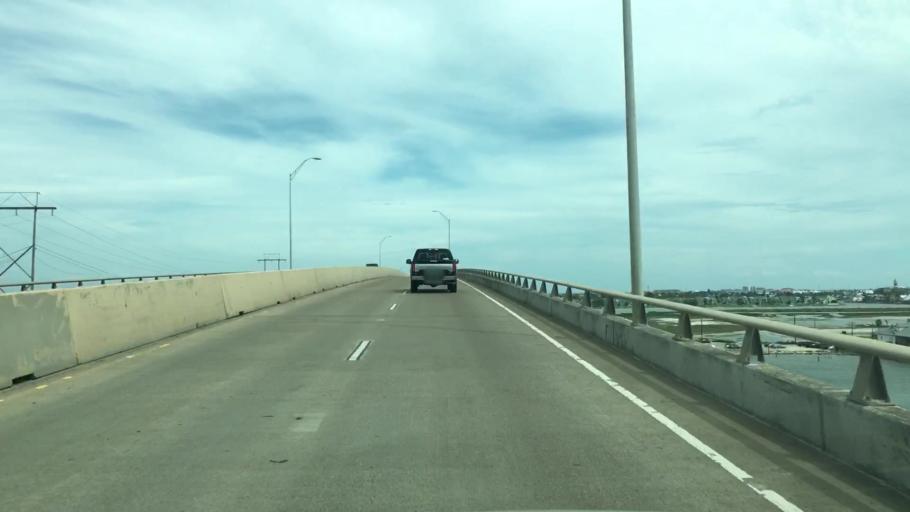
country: US
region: Texas
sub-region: Nueces County
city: Corpus Christi
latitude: 27.6355
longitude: -97.2417
